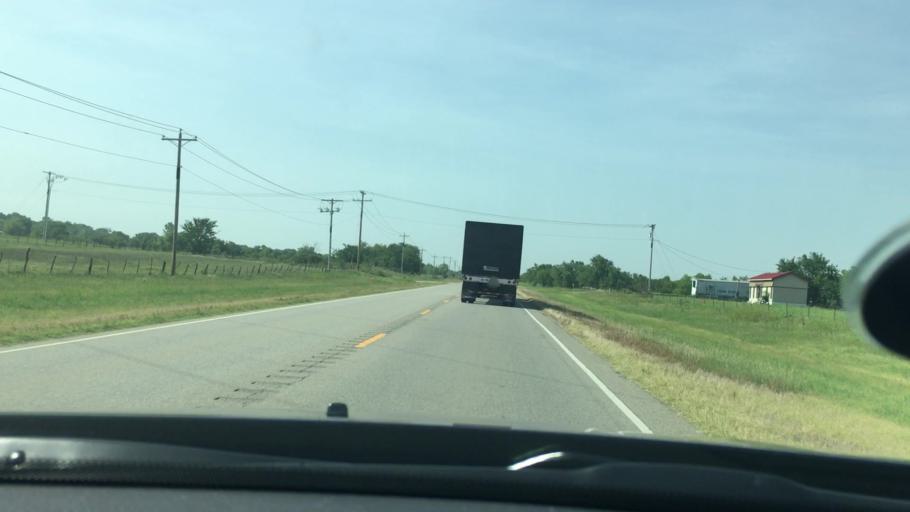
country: US
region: Oklahoma
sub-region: Coal County
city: Coalgate
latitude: 34.4853
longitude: -96.2186
